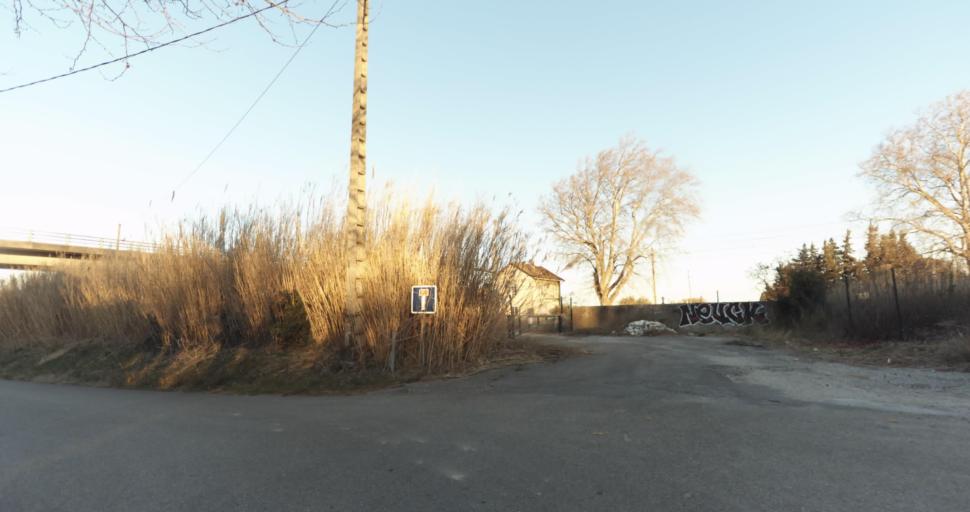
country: FR
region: Provence-Alpes-Cote d'Azur
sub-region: Departement des Bouches-du-Rhone
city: Rognonas
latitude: 43.8965
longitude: 4.7822
